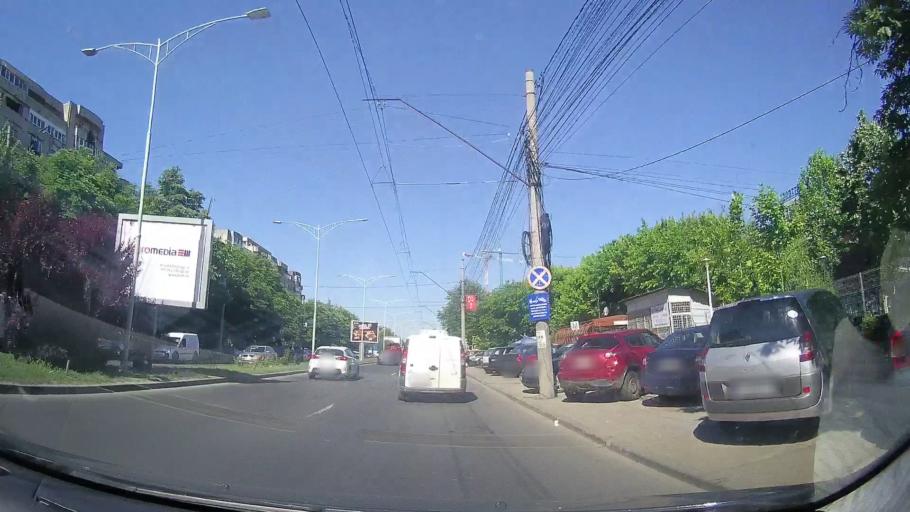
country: RO
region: Ilfov
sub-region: Comuna Chiajna
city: Rosu
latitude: 44.4339
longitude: 26.0036
